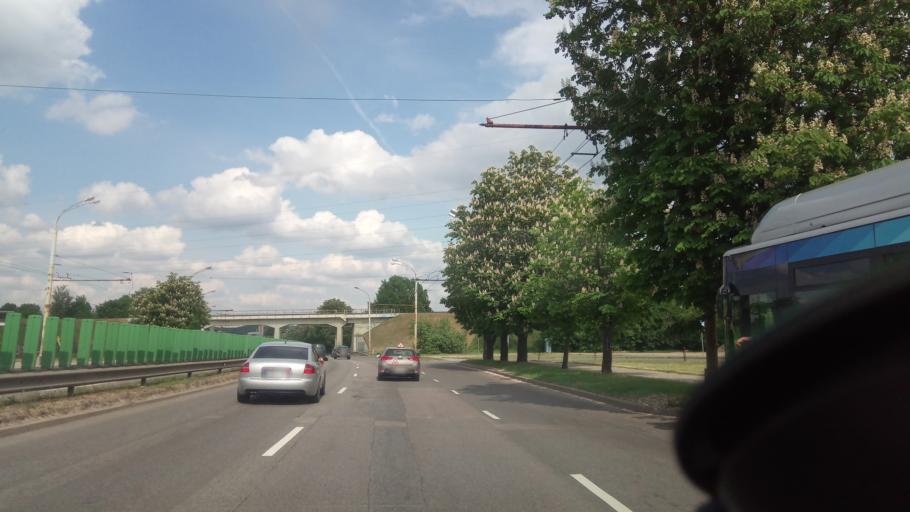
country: LT
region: Vilnius County
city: Lazdynai
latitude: 54.6452
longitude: 25.2024
